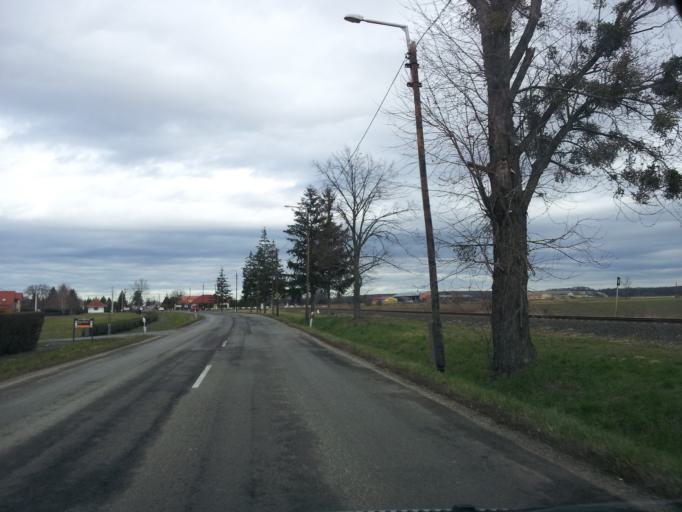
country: HU
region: Vas
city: Gencsapati
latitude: 47.3348
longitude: 16.5825
